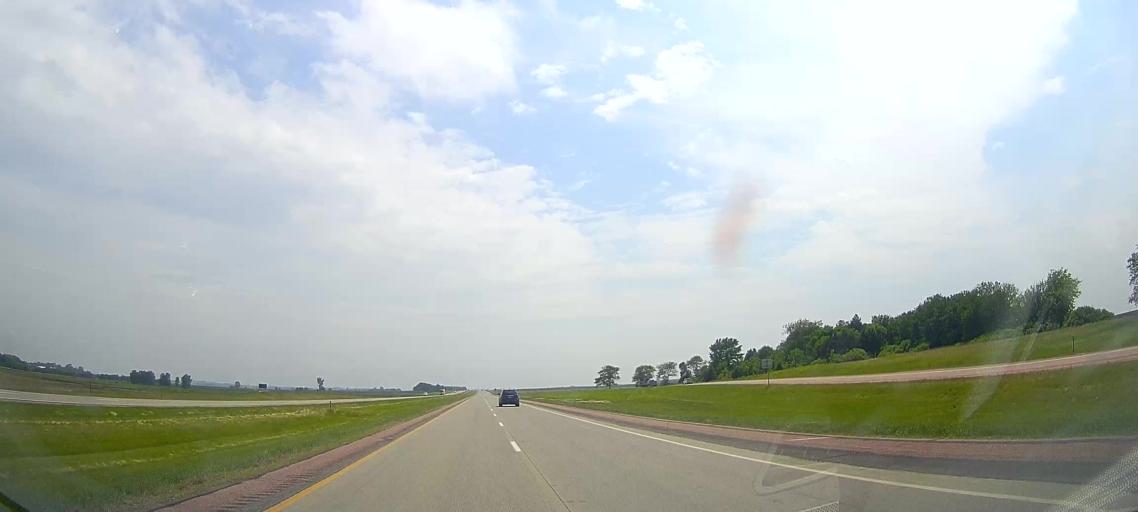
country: US
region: South Dakota
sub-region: Union County
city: Beresford
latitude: 42.9910
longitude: -96.7957
